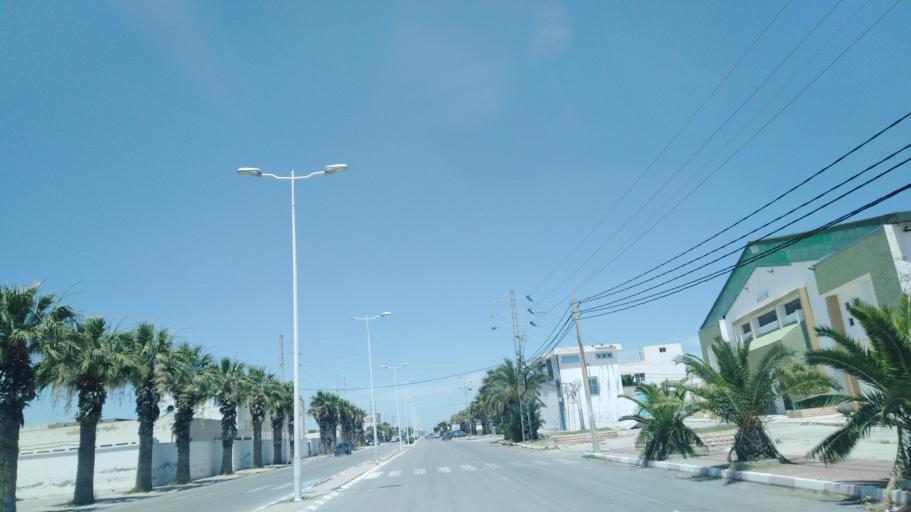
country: TN
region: Al Mahdiyah
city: Ksour Essaf
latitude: 35.4244
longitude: 10.9968
